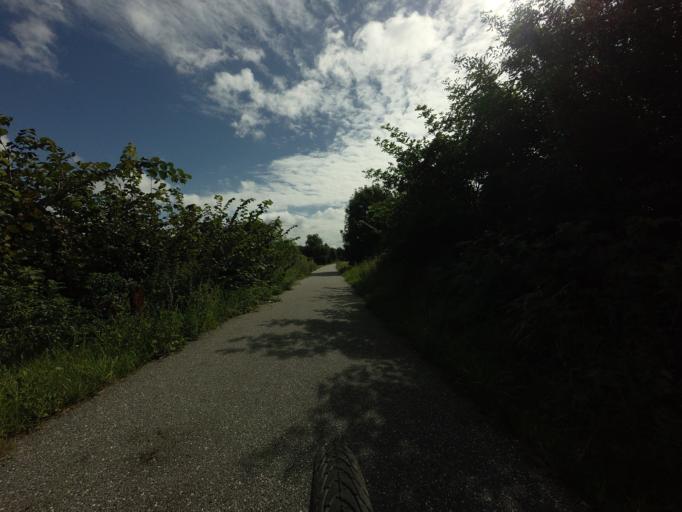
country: DK
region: Central Jutland
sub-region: Norddjurs Kommune
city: Allingabro
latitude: 56.4623
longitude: 10.3339
